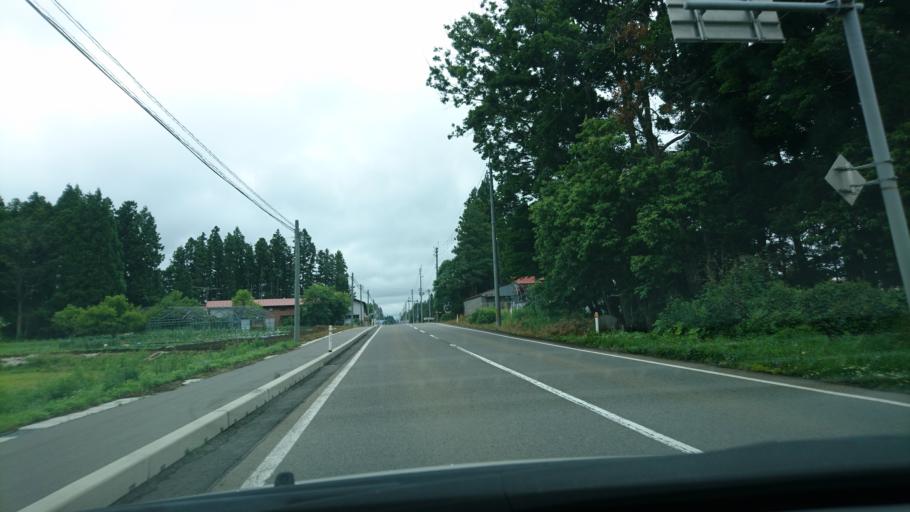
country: JP
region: Iwate
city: Mizusawa
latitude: 39.1032
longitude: 141.0515
